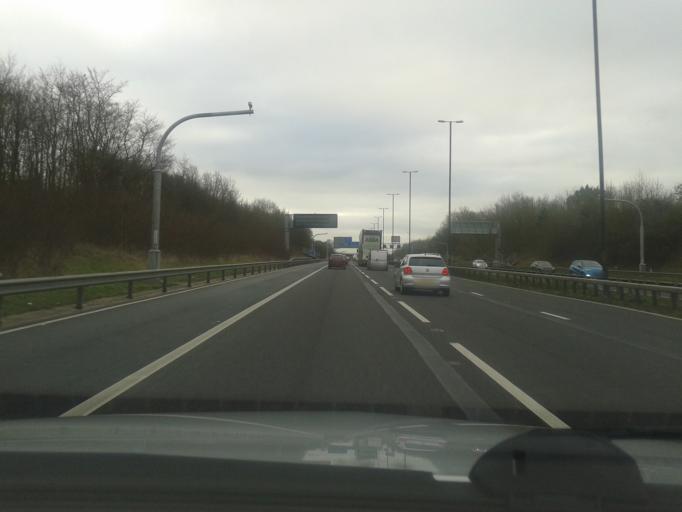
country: GB
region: England
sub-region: South Gloucestershire
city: Stoke Gifford
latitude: 51.5303
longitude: -2.5321
